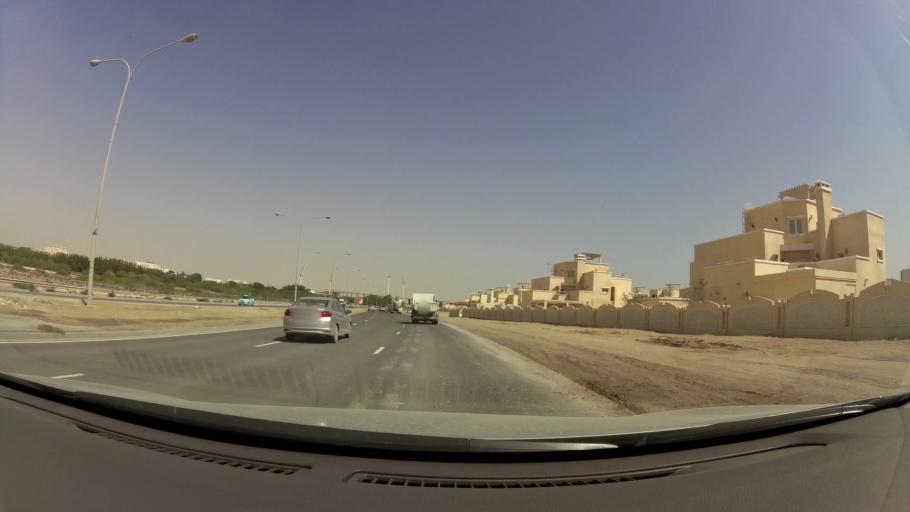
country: QA
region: Baladiyat ad Dawhah
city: Doha
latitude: 25.3692
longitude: 51.4976
